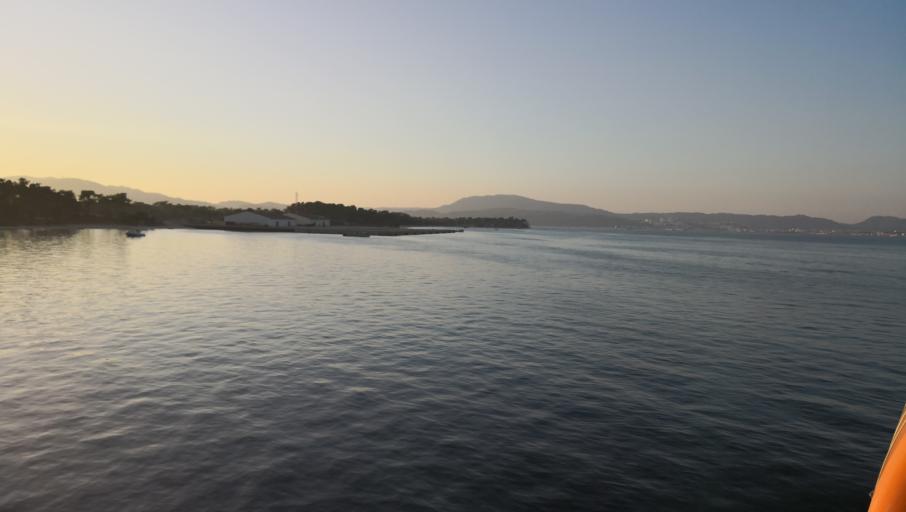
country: PT
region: Setubal
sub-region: Setubal
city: Setubal
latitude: 38.4716
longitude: -8.8654
